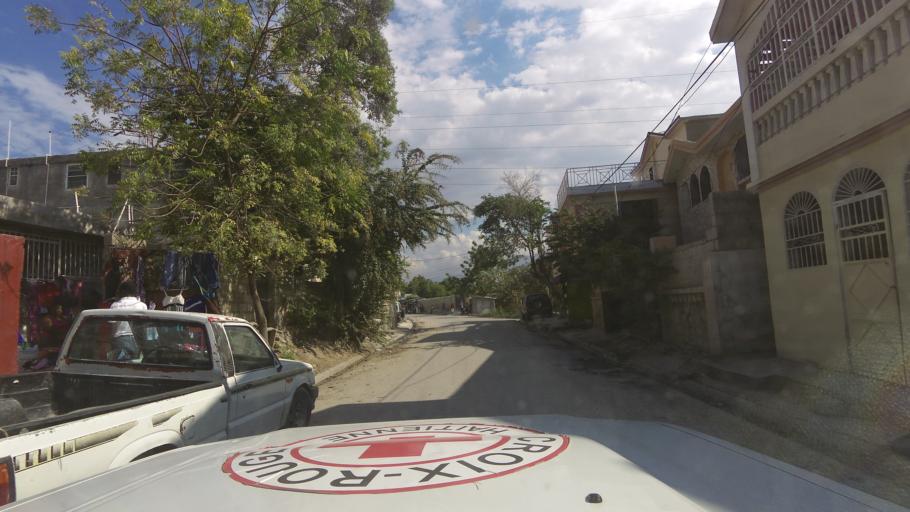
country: HT
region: Ouest
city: Delmas 73
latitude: 18.5599
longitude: -72.2932
